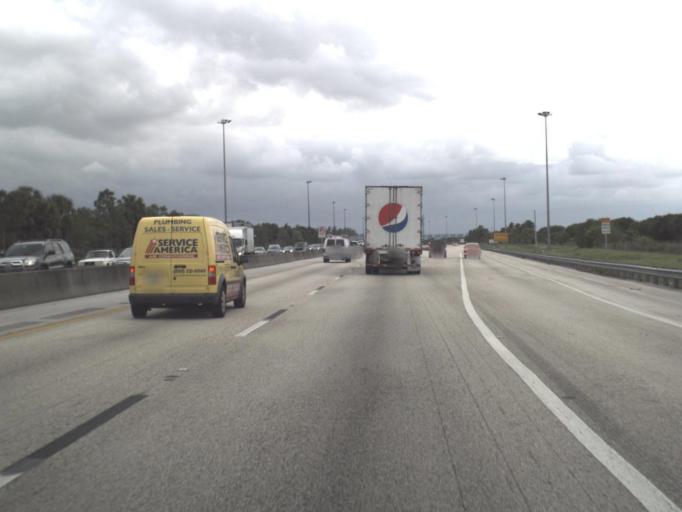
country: US
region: Florida
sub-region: Palm Beach County
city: Greenacres City
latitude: 26.5695
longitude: -80.1732
